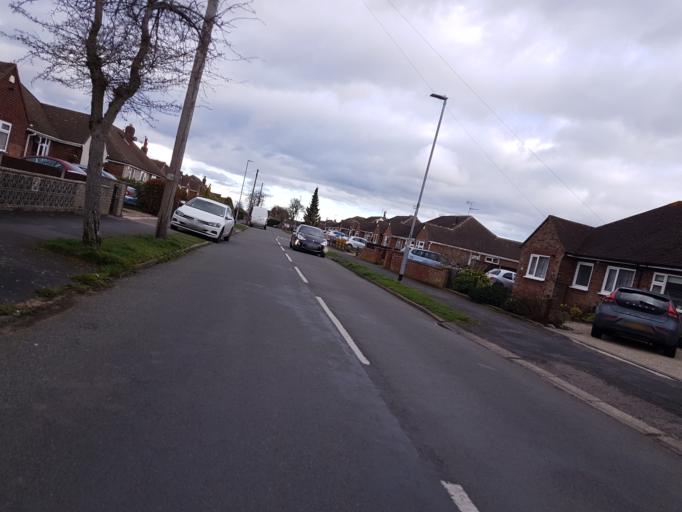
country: GB
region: England
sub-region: Leicestershire
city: Earl Shilton
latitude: 52.5703
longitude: -1.3216
